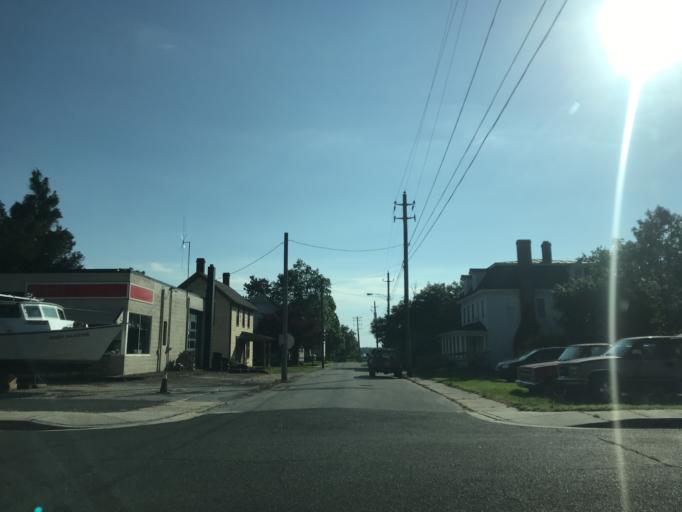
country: US
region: Maryland
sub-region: Wicomico County
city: Hebron
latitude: 38.5426
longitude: -75.7189
